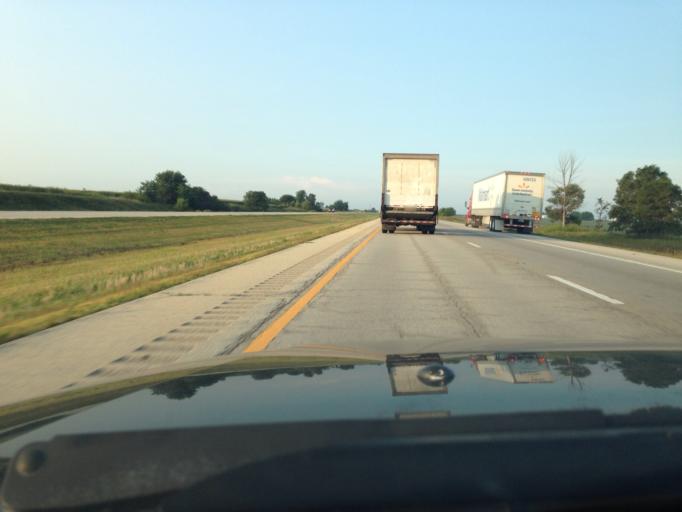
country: US
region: Illinois
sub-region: Ford County
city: Paxton
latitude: 40.5003
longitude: -88.0890
